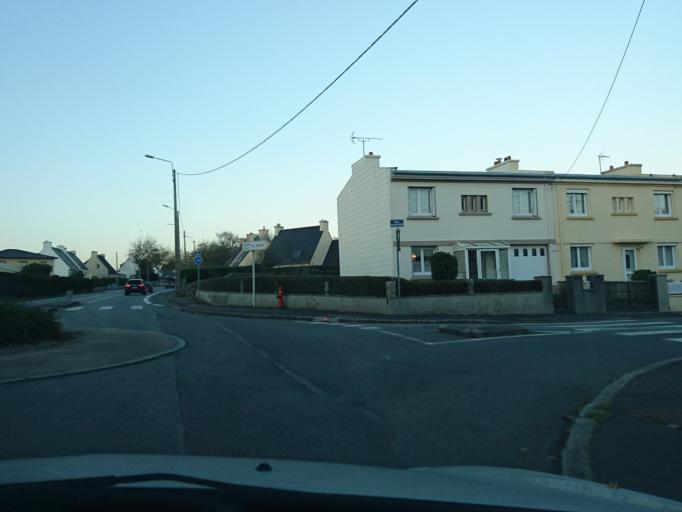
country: FR
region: Brittany
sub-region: Departement du Finistere
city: Brest
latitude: 48.4216
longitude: -4.4864
